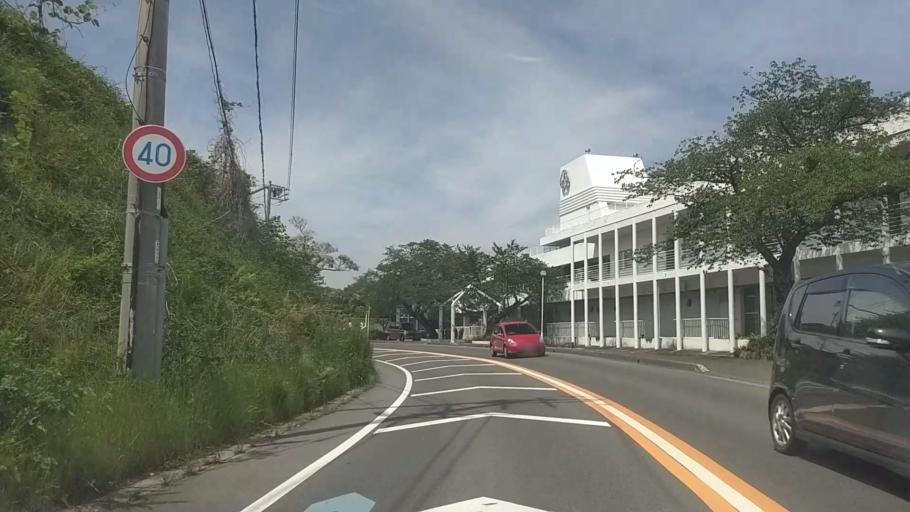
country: JP
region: Shizuoka
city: Kosai-shi
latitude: 34.7738
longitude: 137.5468
